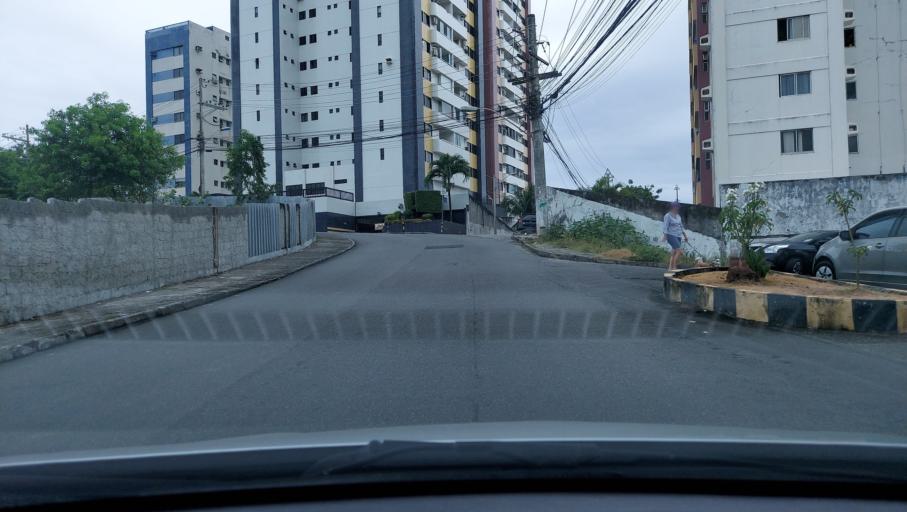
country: BR
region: Bahia
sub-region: Salvador
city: Salvador
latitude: -12.9838
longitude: -38.4425
